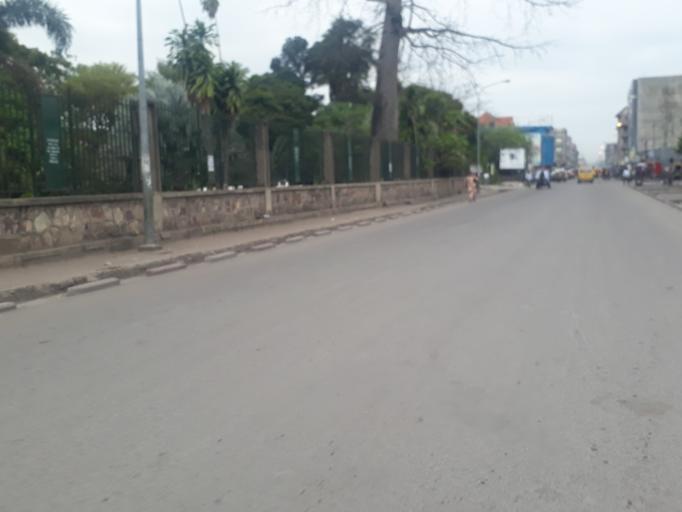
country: CD
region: Kinshasa
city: Kinshasa
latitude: -4.3107
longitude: 15.3086
